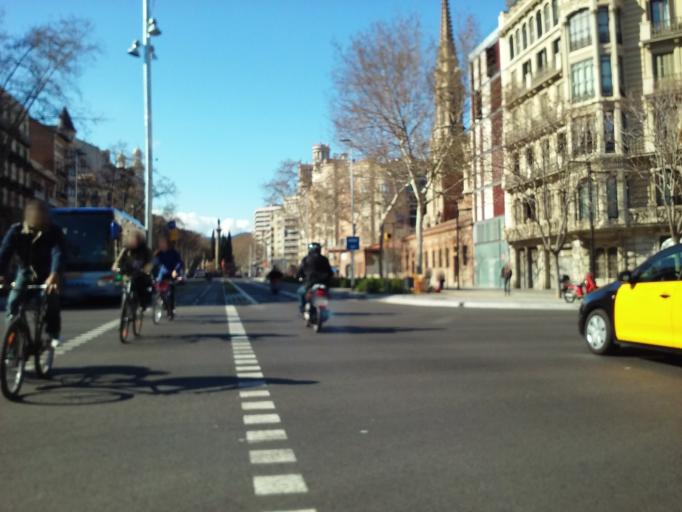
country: ES
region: Catalonia
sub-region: Provincia de Barcelona
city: Eixample
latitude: 41.3976
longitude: 2.1722
